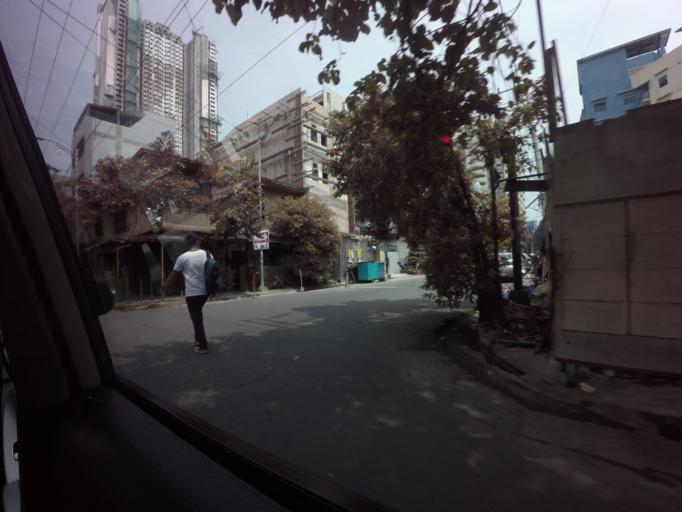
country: PH
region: Metro Manila
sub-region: City of Manila
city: Port Area
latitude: 14.5746
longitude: 120.9910
